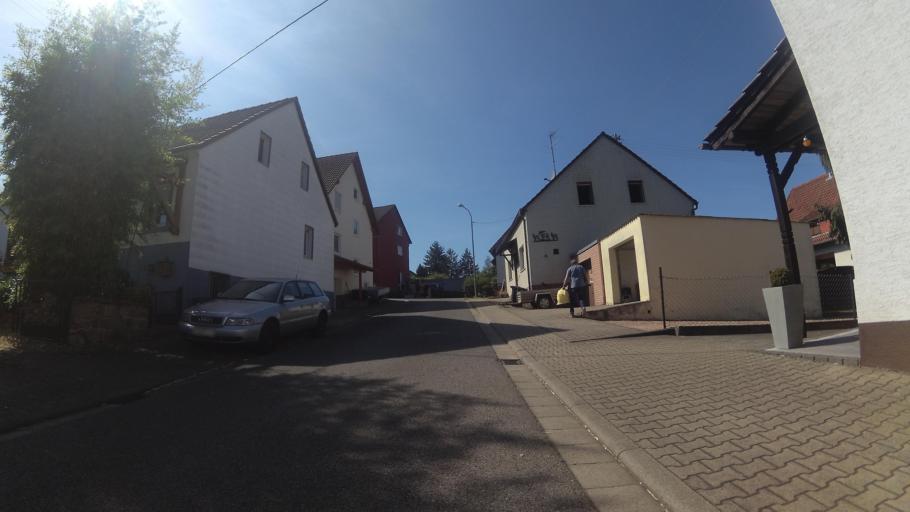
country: DE
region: Rheinland-Pfalz
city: Dittweiler
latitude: 49.4081
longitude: 7.3372
